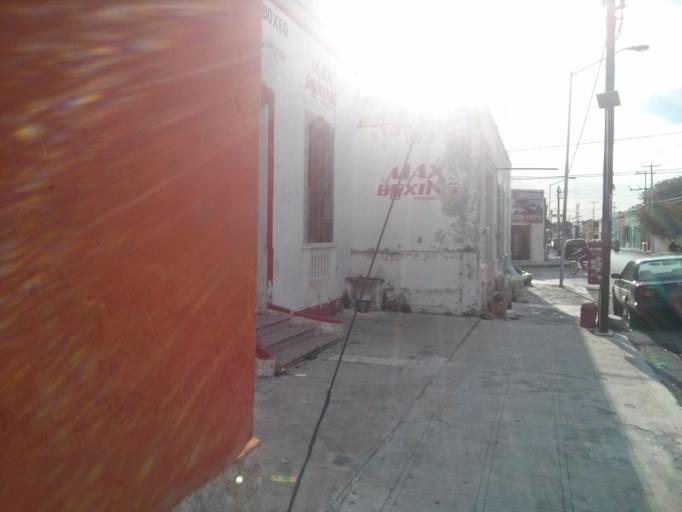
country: MX
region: Yucatan
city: Merida
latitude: 20.9654
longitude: -89.6112
